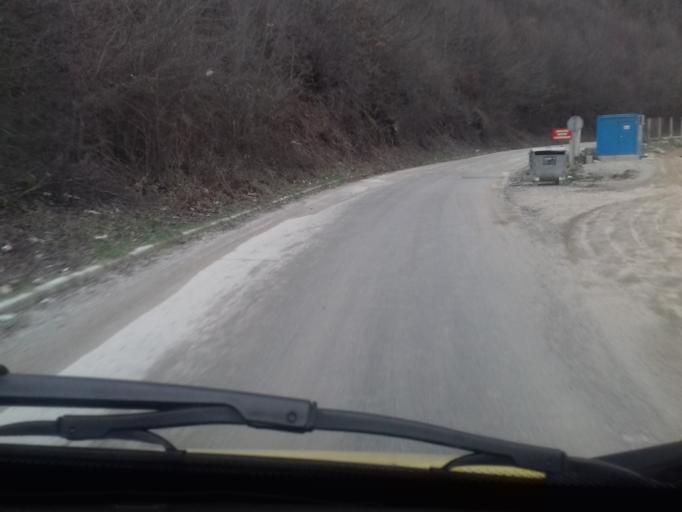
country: BA
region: Federation of Bosnia and Herzegovina
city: Zenica
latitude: 44.2161
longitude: 17.9480
